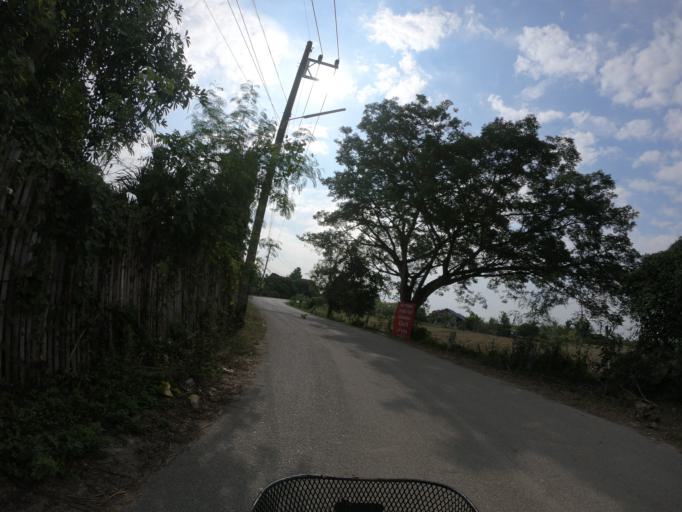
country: TH
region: Chiang Mai
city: Saraphi
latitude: 18.7413
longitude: 99.0615
